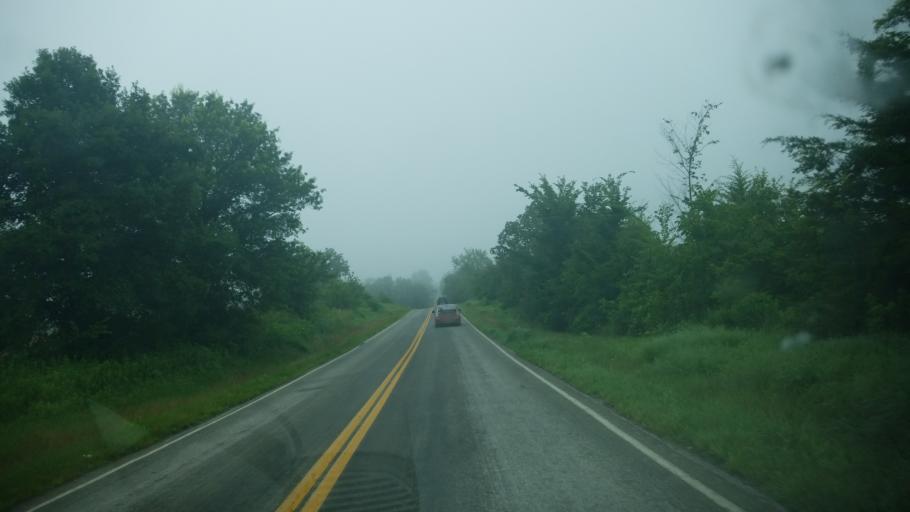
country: US
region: Missouri
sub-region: Audrain County
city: Vandalia
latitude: 39.3148
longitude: -91.3449
